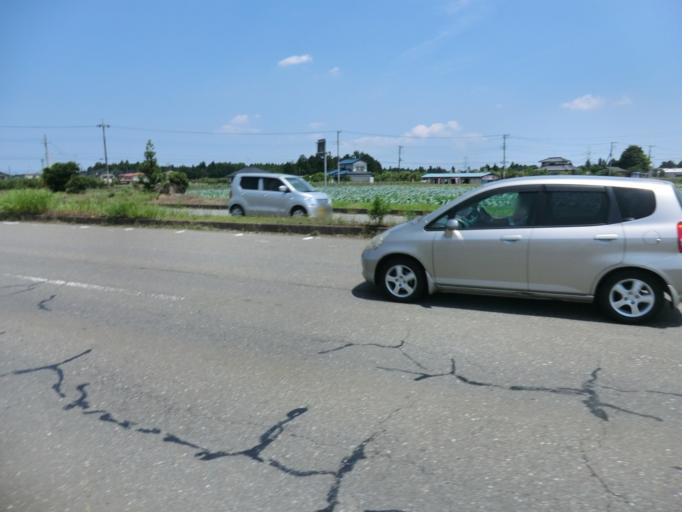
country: JP
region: Ibaraki
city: Ushiku
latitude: 36.0053
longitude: 140.0821
